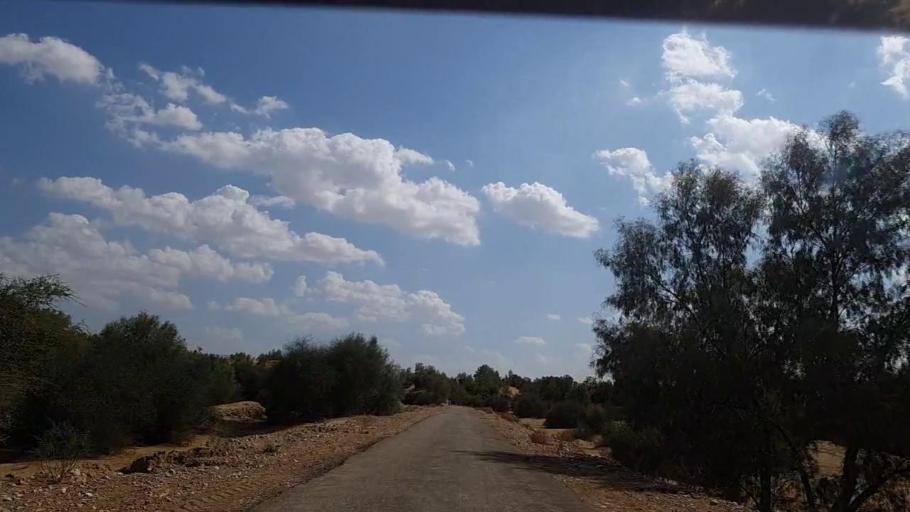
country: PK
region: Sindh
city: Johi
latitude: 26.5183
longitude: 67.4518
